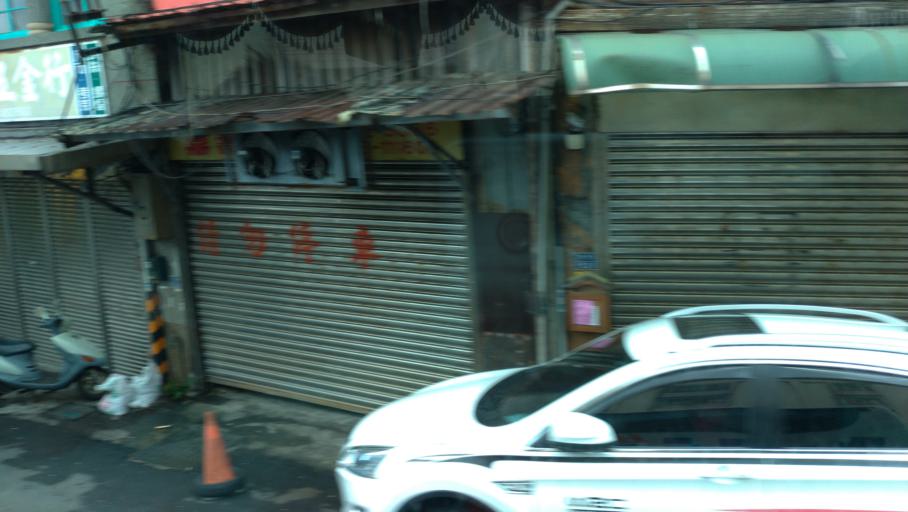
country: TW
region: Taiwan
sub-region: Keelung
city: Keelung
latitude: 25.1526
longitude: 121.7684
